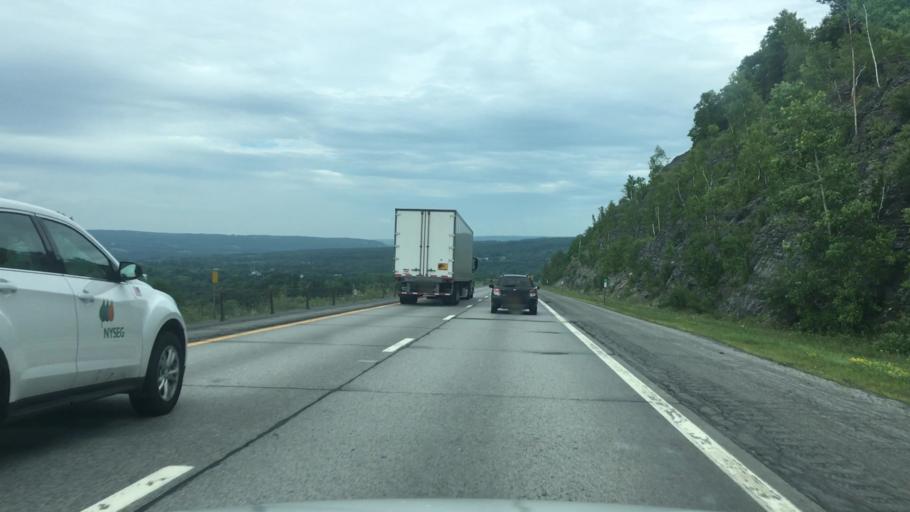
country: US
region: New York
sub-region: Schoharie County
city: Schoharie
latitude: 42.6935
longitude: -74.3510
